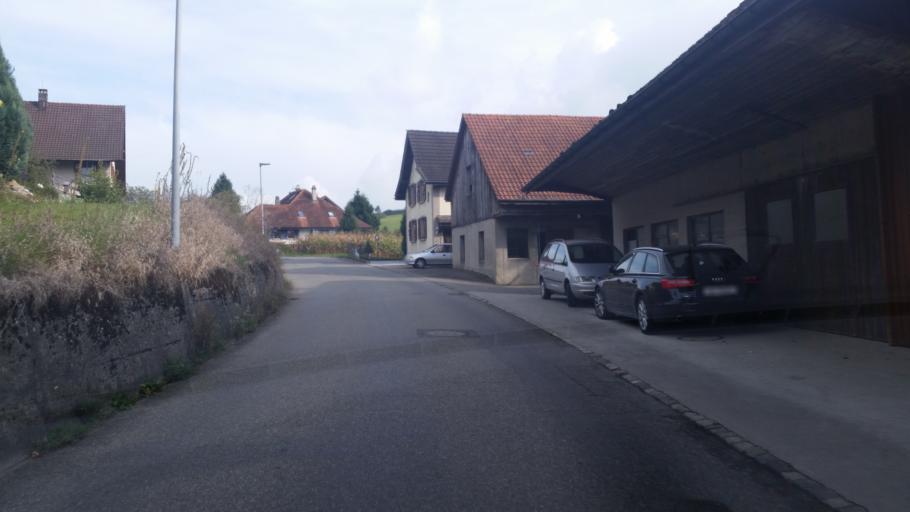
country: CH
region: Aargau
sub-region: Bezirk Bremgarten
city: Hagglingen
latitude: 47.3885
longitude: 8.2551
